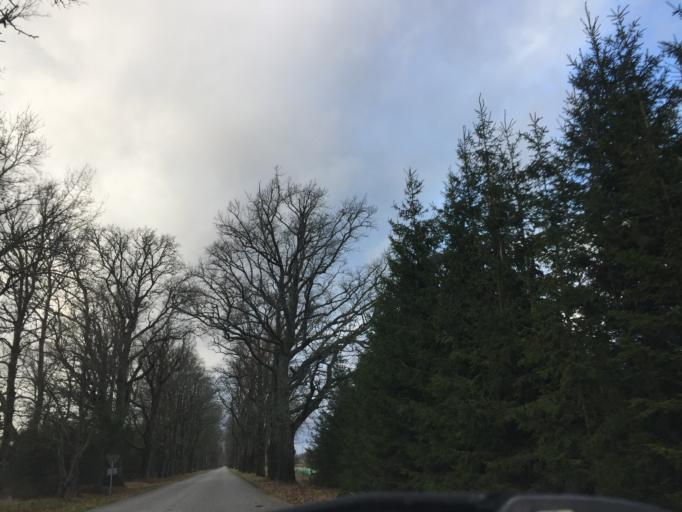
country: LV
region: Burtnieki
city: Matisi
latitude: 57.6852
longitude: 25.2897
